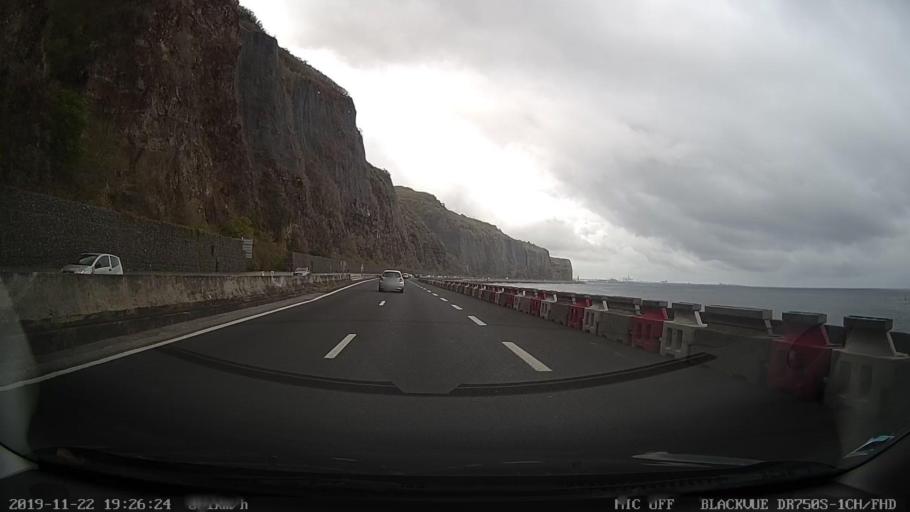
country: RE
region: Reunion
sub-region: Reunion
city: La Possession
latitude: -20.9007
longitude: 55.3679
